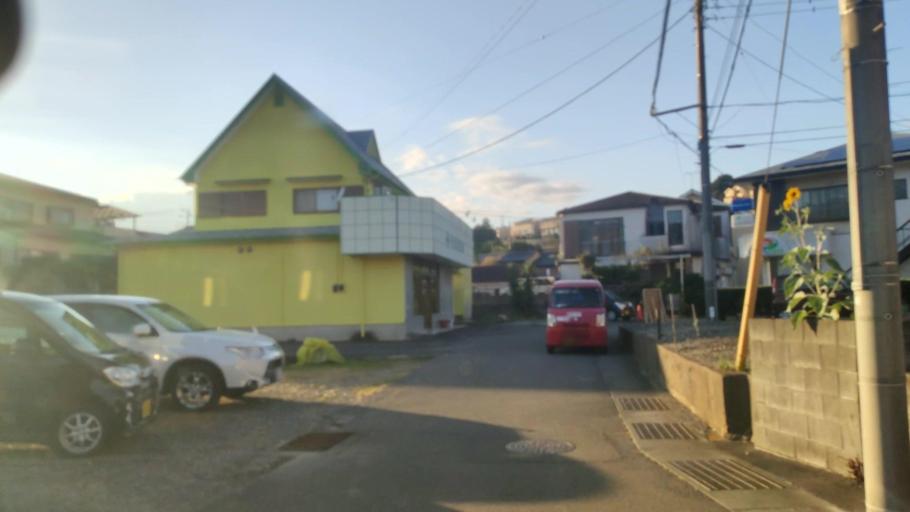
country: JP
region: Shizuoka
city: Ito
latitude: 34.9500
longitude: 139.1226
